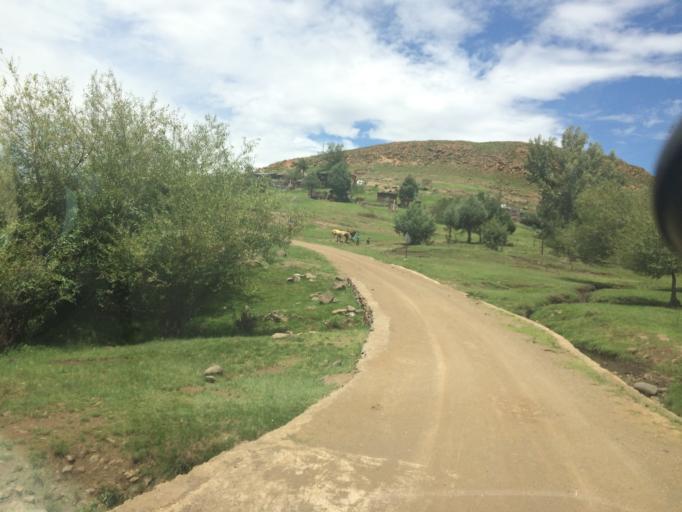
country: LS
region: Maseru
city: Nako
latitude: -29.8645
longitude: 28.0376
